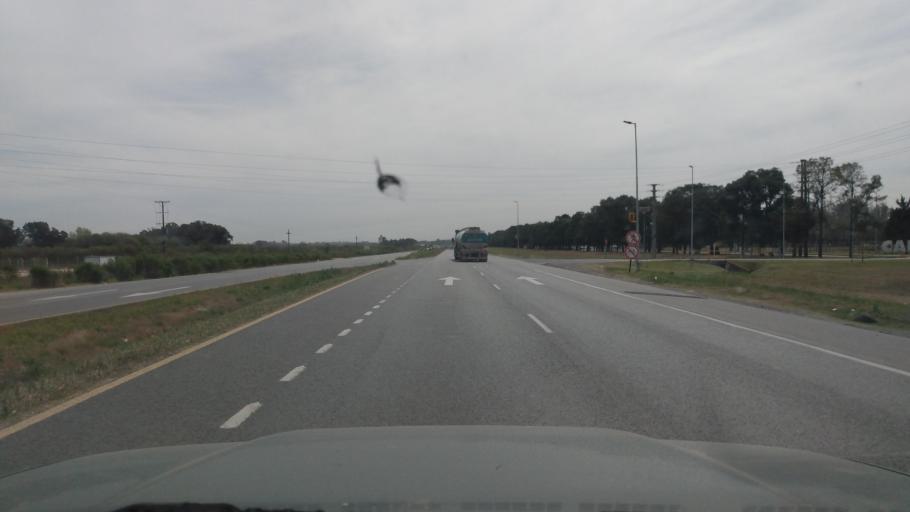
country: AR
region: Buenos Aires
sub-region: Partido de Lujan
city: Lujan
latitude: -34.5387
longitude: -59.0370
